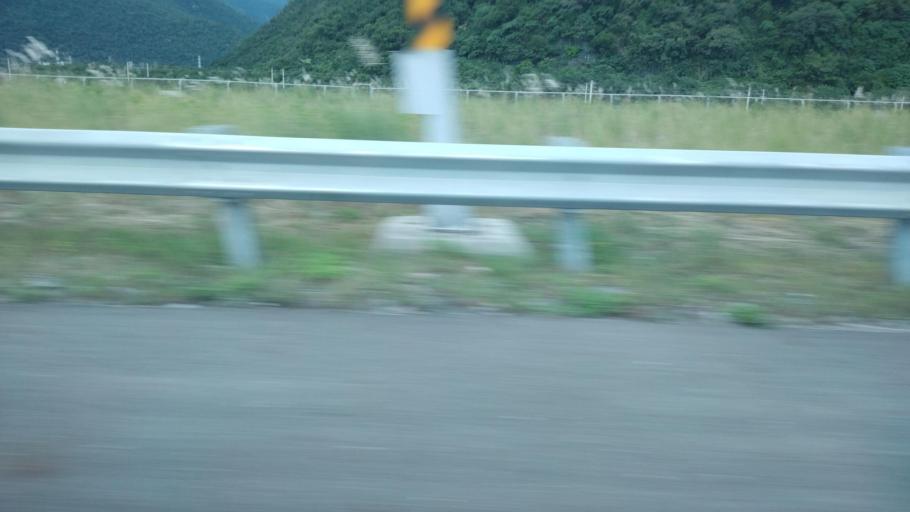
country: TW
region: Taiwan
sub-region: Hualien
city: Hualian
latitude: 24.3214
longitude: 121.7650
